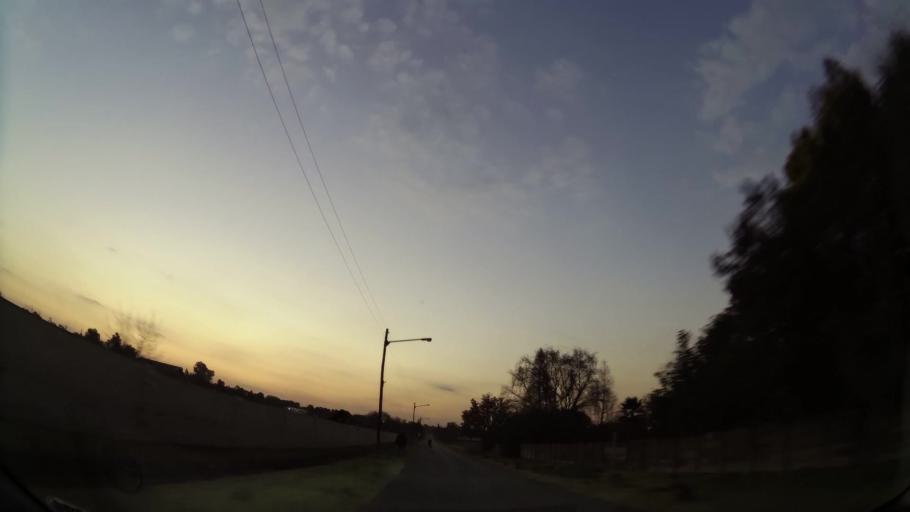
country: ZA
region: Gauteng
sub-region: Ekurhuleni Metropolitan Municipality
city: Benoni
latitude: -26.1290
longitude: 28.3094
